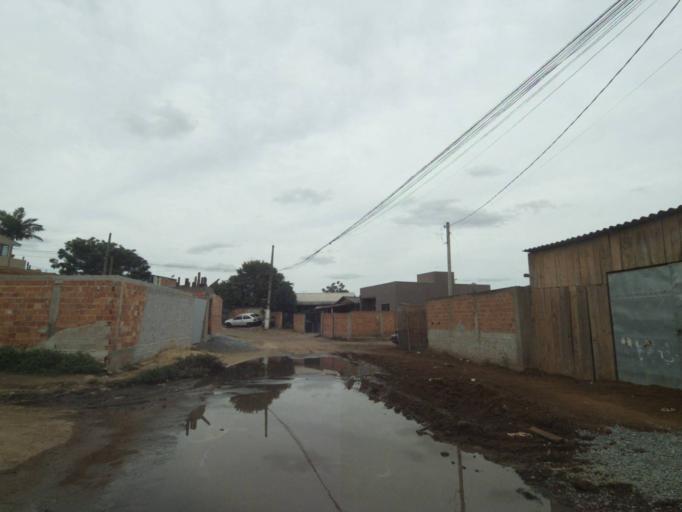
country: BR
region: Parana
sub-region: Curitiba
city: Curitiba
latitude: -25.5087
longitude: -49.3383
